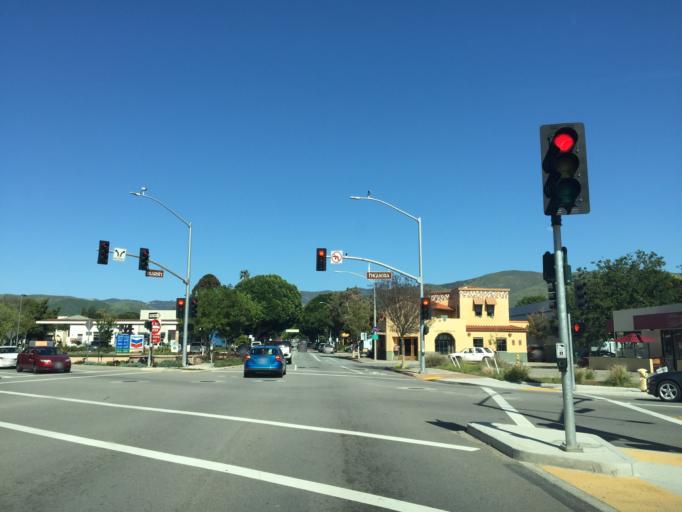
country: US
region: California
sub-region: San Luis Obispo County
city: San Luis Obispo
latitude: 35.2747
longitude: -120.6695
